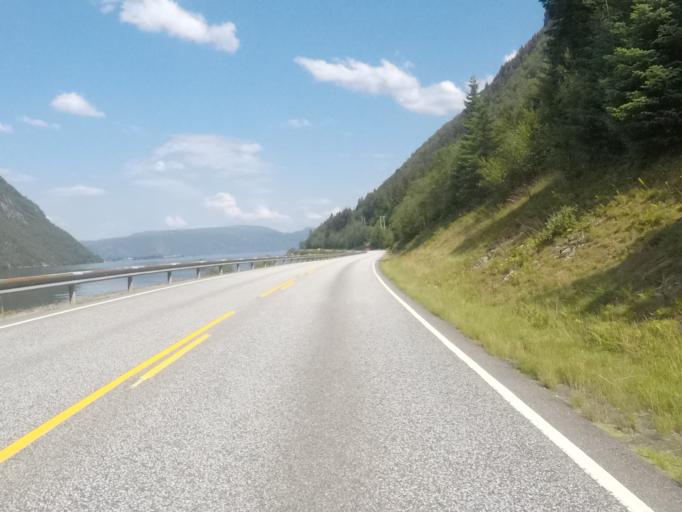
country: NO
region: Sogn og Fjordane
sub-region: Hyllestad
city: Hyllestad
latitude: 60.9905
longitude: 5.4863
